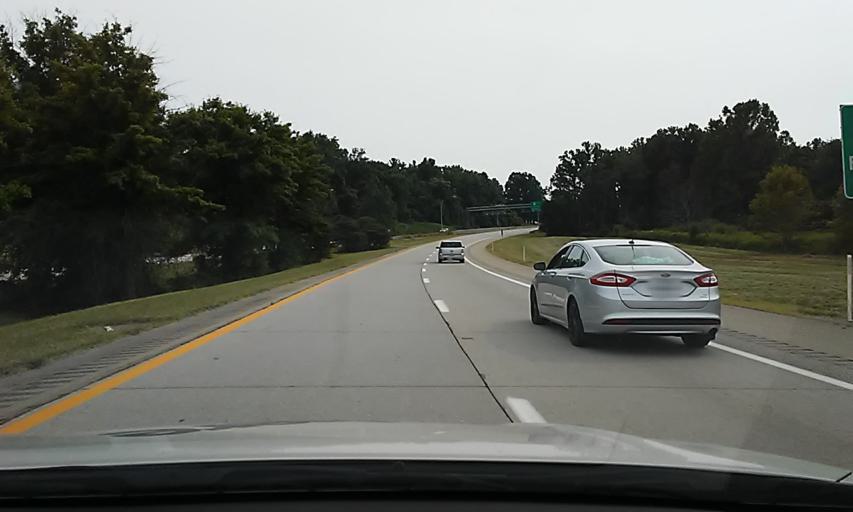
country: US
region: Pennsylvania
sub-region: Fayette County
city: Leith-Hatfield
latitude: 39.8711
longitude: -79.7450
